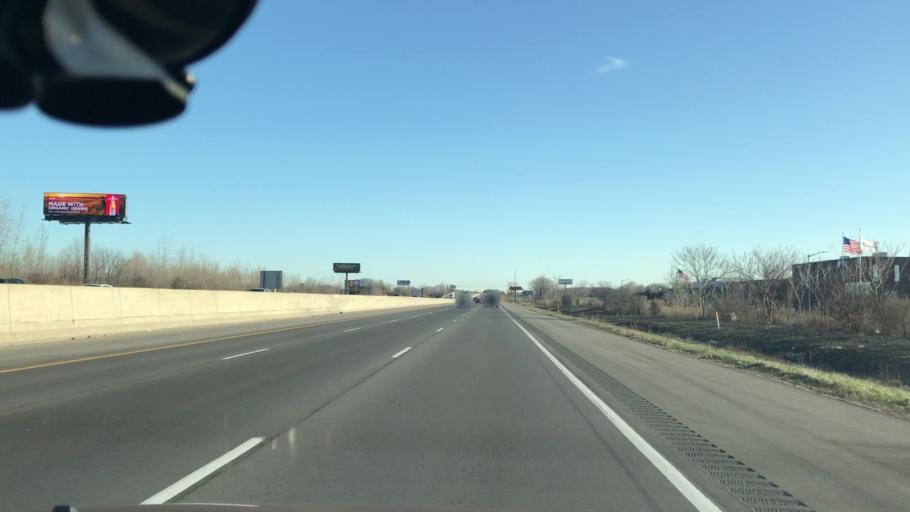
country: US
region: Michigan
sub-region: Macomb County
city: Mount Clemens
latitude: 42.6025
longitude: -82.8563
